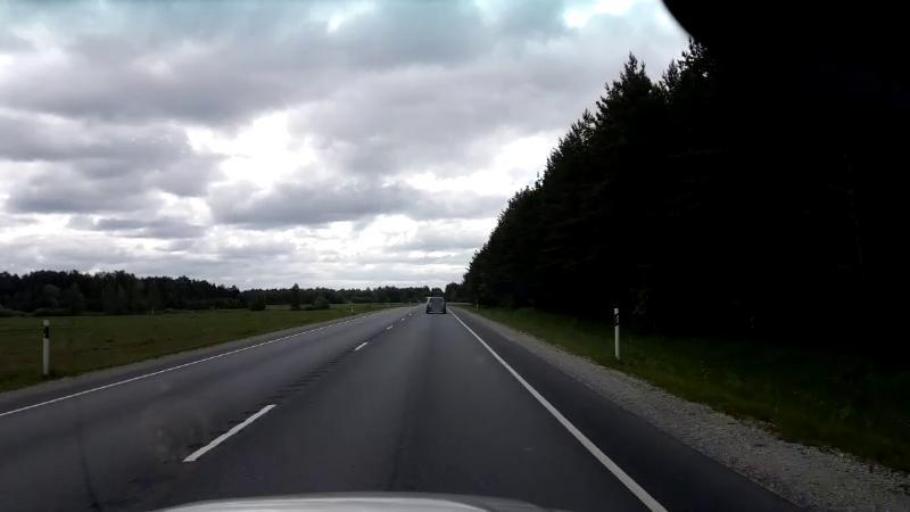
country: EE
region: Paernumaa
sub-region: Halinga vald
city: Parnu-Jaagupi
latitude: 58.6620
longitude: 24.4655
